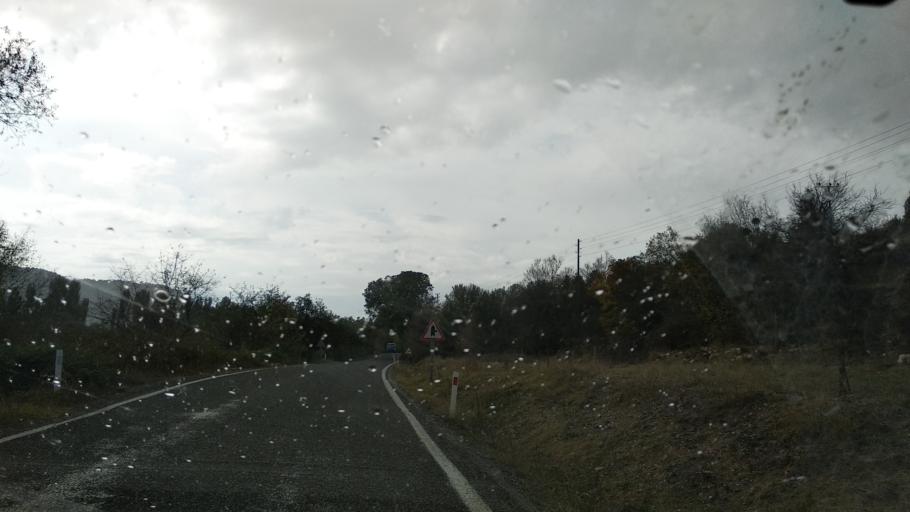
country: TR
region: Ankara
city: Nallihan
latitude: 40.3352
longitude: 31.4161
